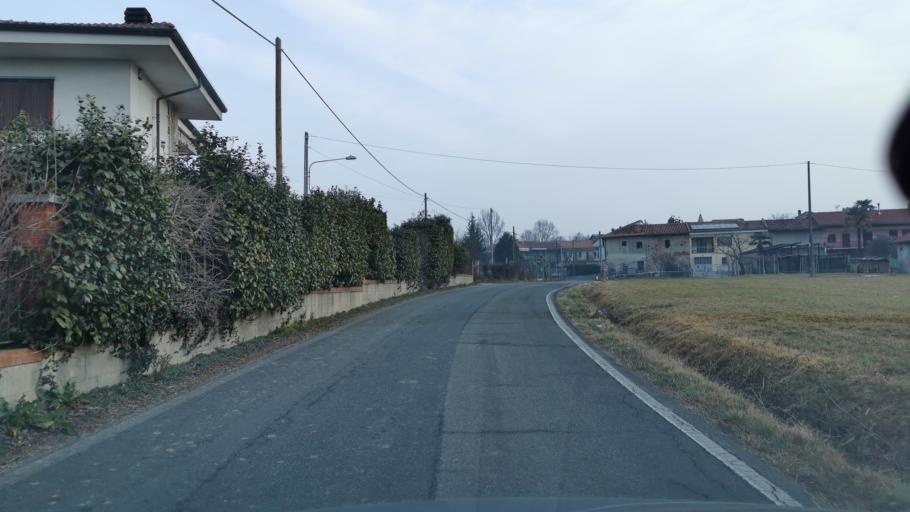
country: IT
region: Piedmont
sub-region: Provincia di Torino
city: Cuceglio
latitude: 45.3493
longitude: 7.8121
